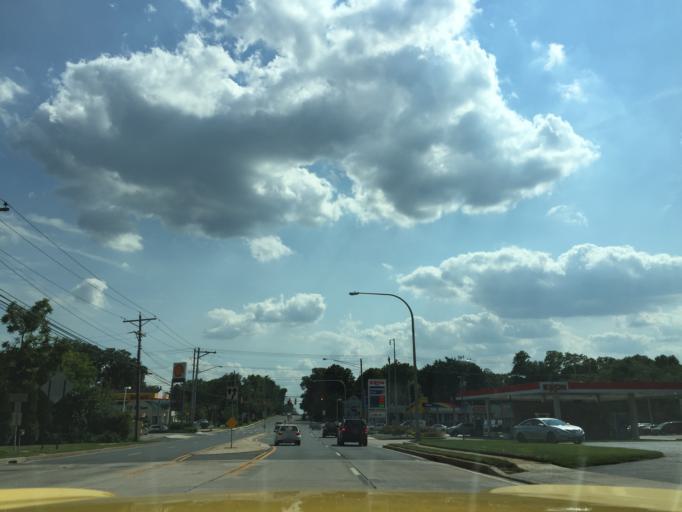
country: US
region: Delaware
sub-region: New Castle County
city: Bellefonte
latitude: 39.8092
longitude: -75.5144
